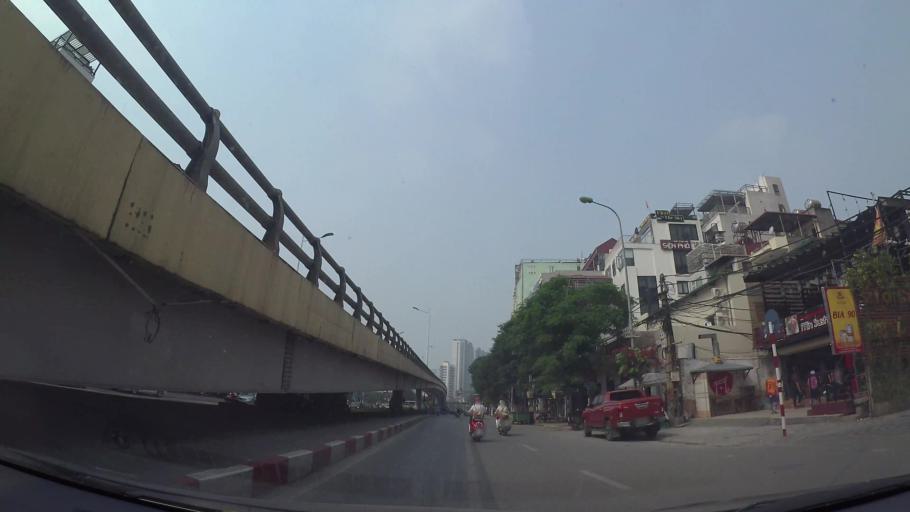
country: VN
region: Ha Noi
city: Thanh Xuan
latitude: 21.0118
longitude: 105.8116
